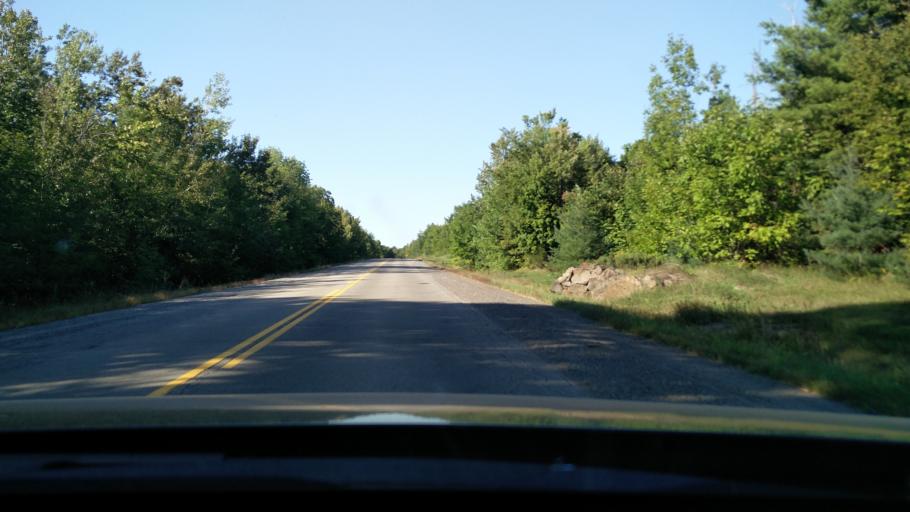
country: CA
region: Ontario
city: Perth
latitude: 44.7116
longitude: -76.4012
